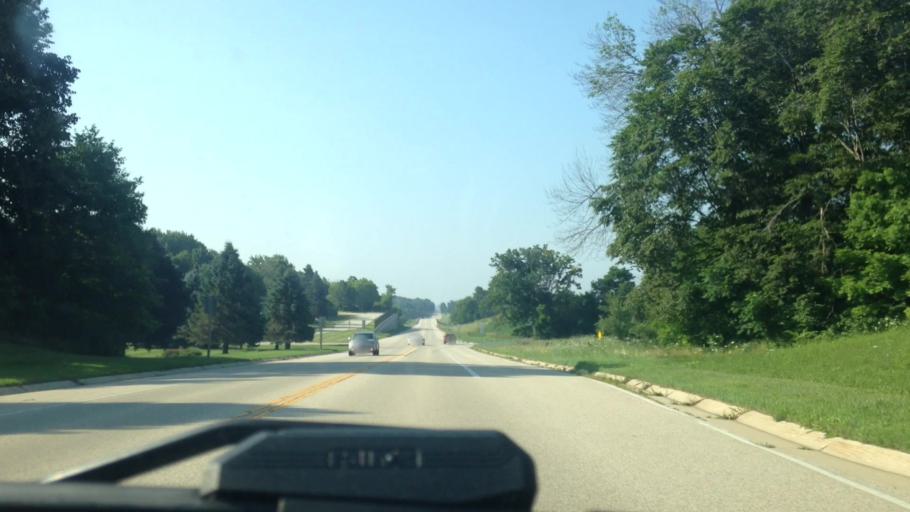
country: US
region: Wisconsin
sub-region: Washington County
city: Slinger
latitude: 43.3178
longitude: -88.2608
